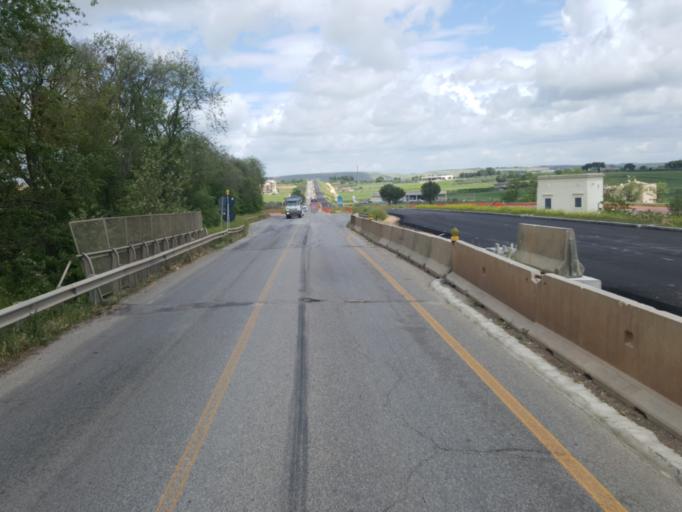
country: IT
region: Apulia
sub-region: Provincia di Bari
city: Altamura
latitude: 40.8234
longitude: 16.5704
